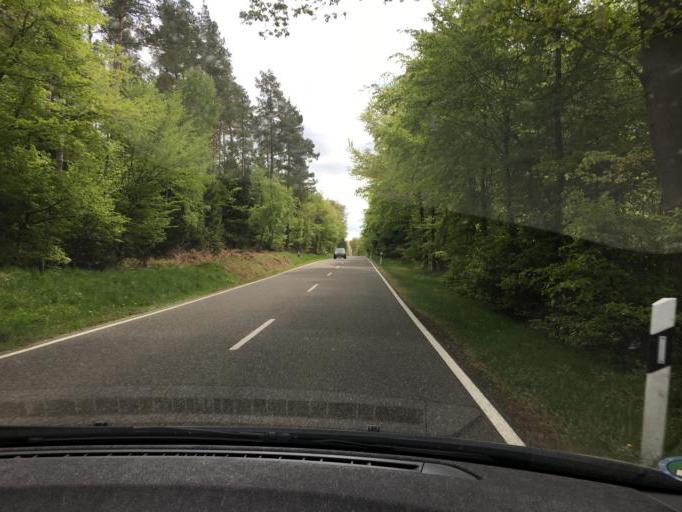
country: DE
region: North Rhine-Westphalia
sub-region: Regierungsbezirk Koln
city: Bad Munstereifel
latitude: 50.5416
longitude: 6.8193
